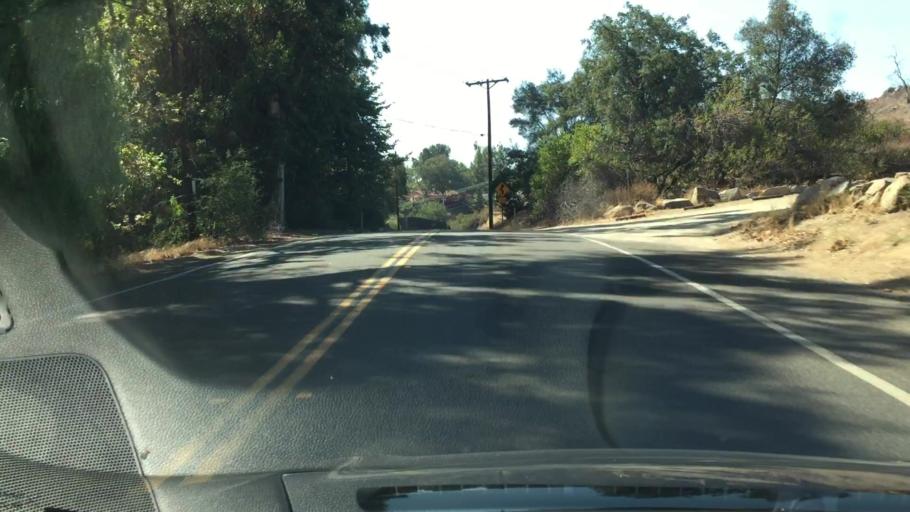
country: US
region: California
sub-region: San Diego County
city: Jamul
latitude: 32.7293
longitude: -116.8725
